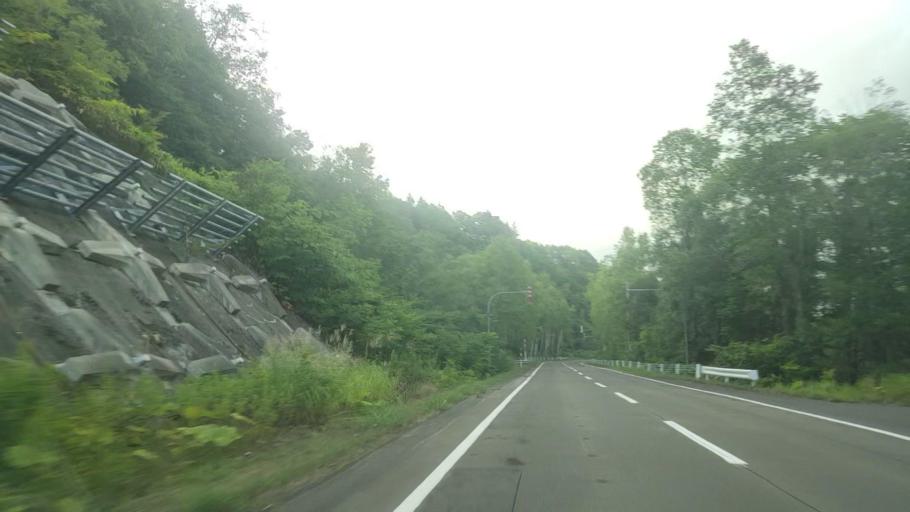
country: JP
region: Hokkaido
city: Bibai
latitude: 43.1327
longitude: 142.0946
